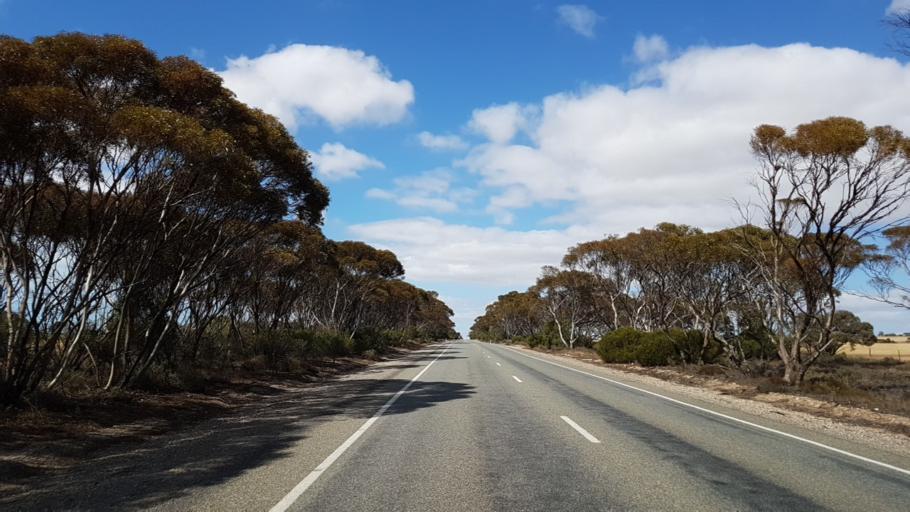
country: AU
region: South Australia
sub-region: Yorke Peninsula
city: Ardrossan
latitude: -34.2837
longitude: 137.9790
